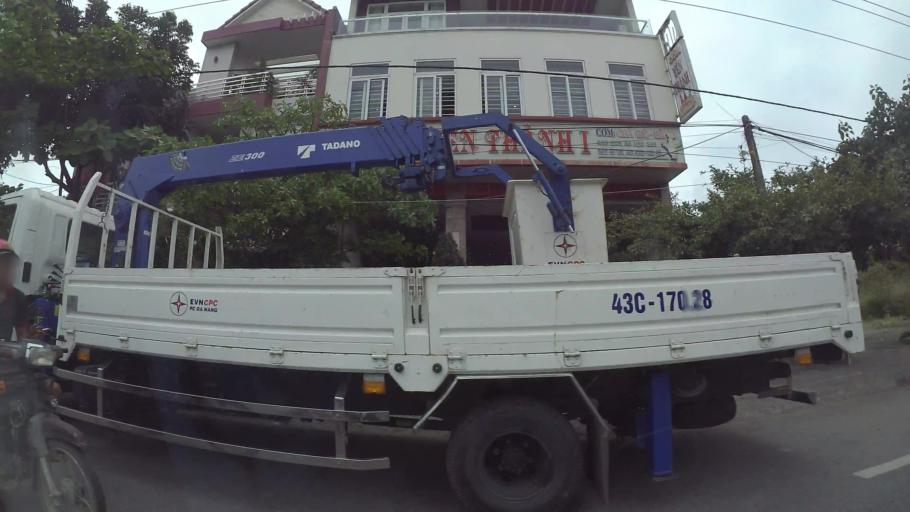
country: VN
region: Da Nang
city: Da Nang
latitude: 16.1035
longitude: 108.2472
